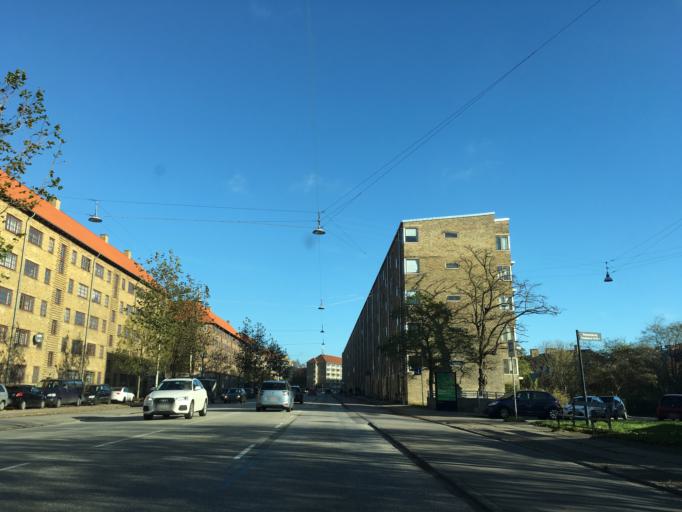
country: DK
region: Capital Region
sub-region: Frederiksberg Kommune
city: Frederiksberg
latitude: 55.7101
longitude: 12.5282
